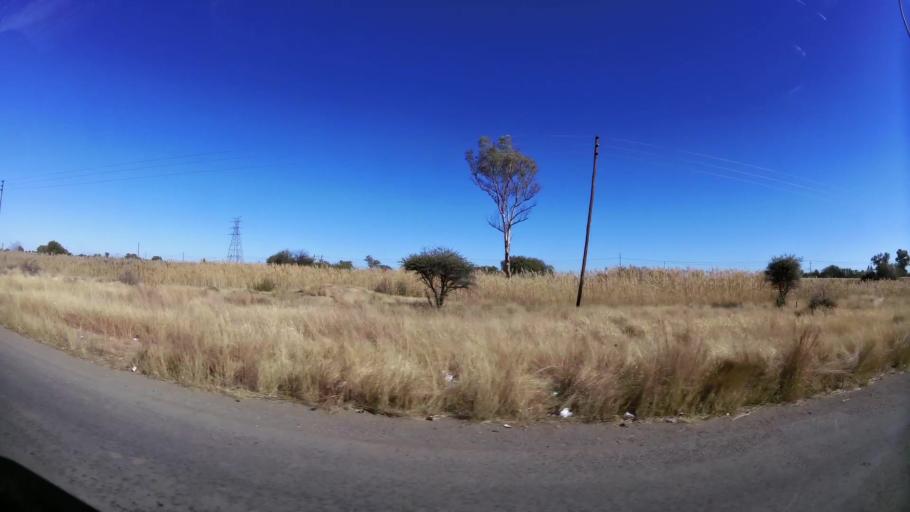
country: ZA
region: Northern Cape
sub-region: Frances Baard District Municipality
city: Kimberley
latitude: -28.7035
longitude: 24.7770
